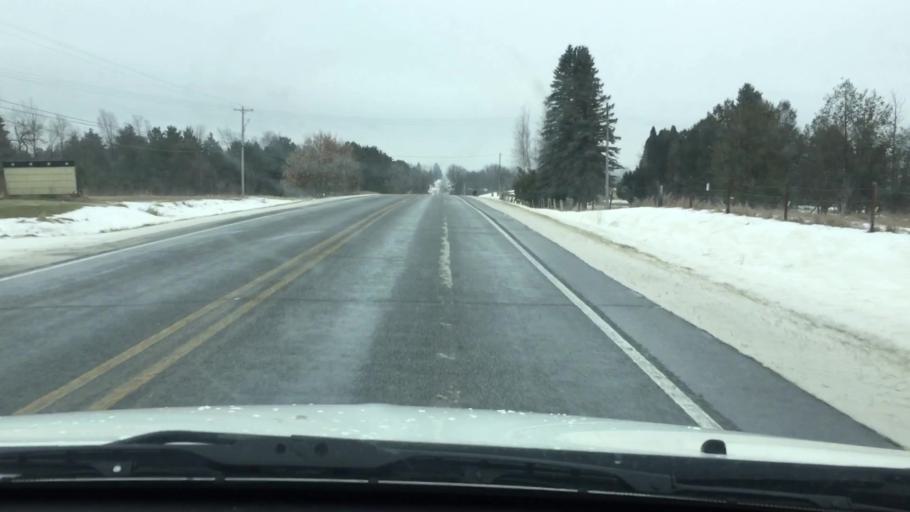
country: US
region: Michigan
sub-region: Wexford County
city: Cadillac
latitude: 44.0800
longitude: -85.4441
